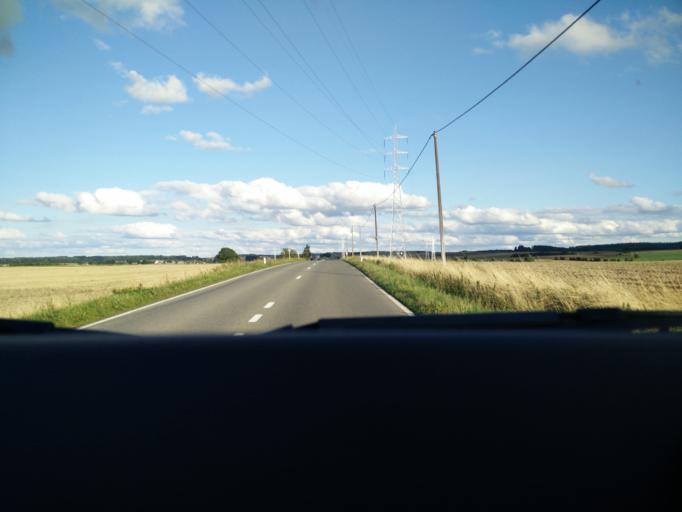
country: BE
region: Wallonia
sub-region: Province de Namur
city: Walcourt
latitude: 50.2214
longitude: 4.4306
